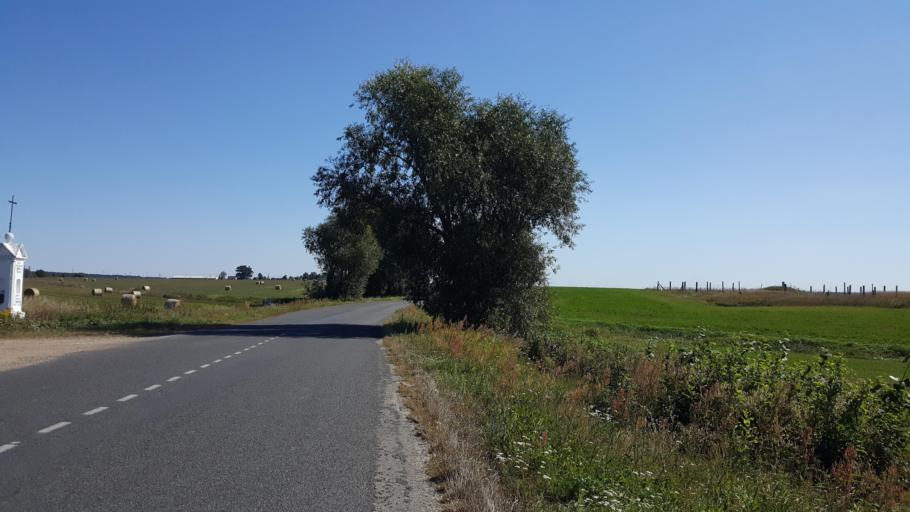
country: PL
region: Lublin Voivodeship
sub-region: Powiat bialski
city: Terespol
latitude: 52.2104
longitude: 23.5267
